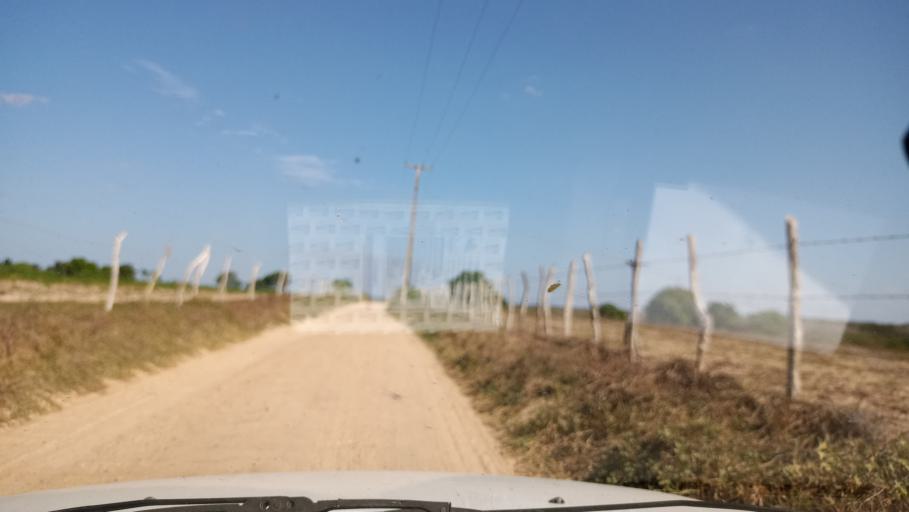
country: BR
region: Rio Grande do Norte
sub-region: Brejinho
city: Brejinho
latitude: -6.1772
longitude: -35.4565
